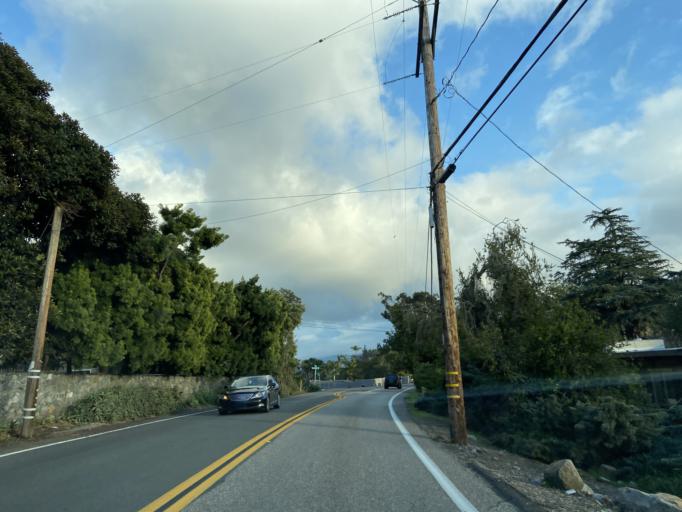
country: US
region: California
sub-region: San Diego County
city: Casa de Oro-Mount Helix
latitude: 32.7748
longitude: -116.9827
